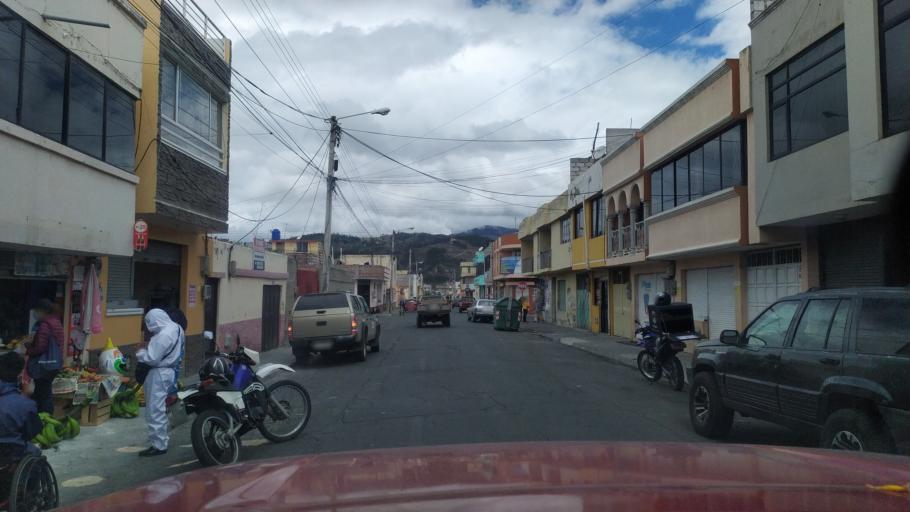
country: EC
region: Chimborazo
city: Riobamba
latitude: -1.6768
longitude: -78.6492
